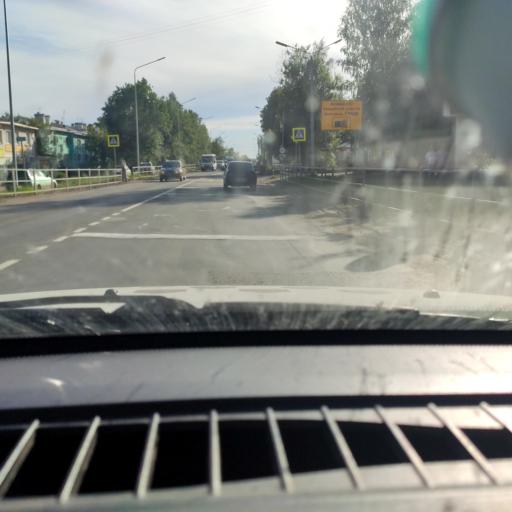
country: RU
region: Kirov
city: Vakhrushi
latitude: 58.6800
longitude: 50.0271
